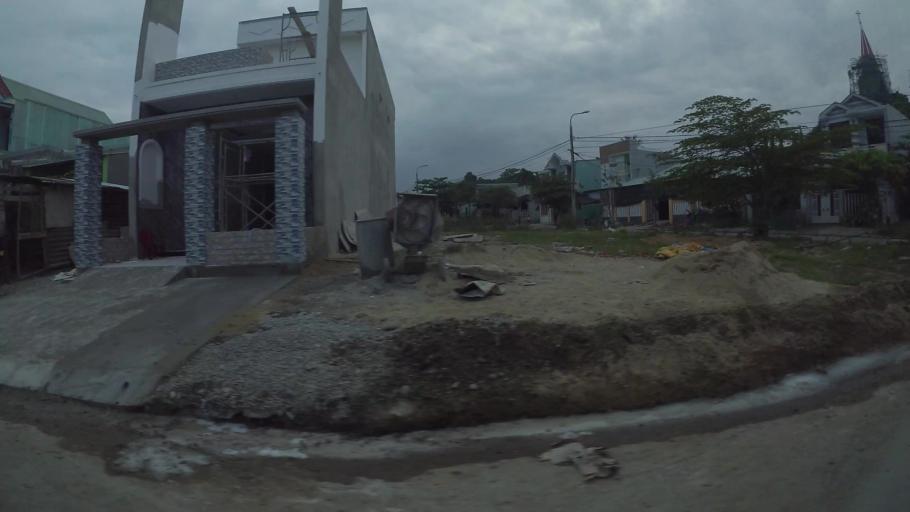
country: VN
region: Da Nang
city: Lien Chieu
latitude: 16.0675
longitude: 108.1042
